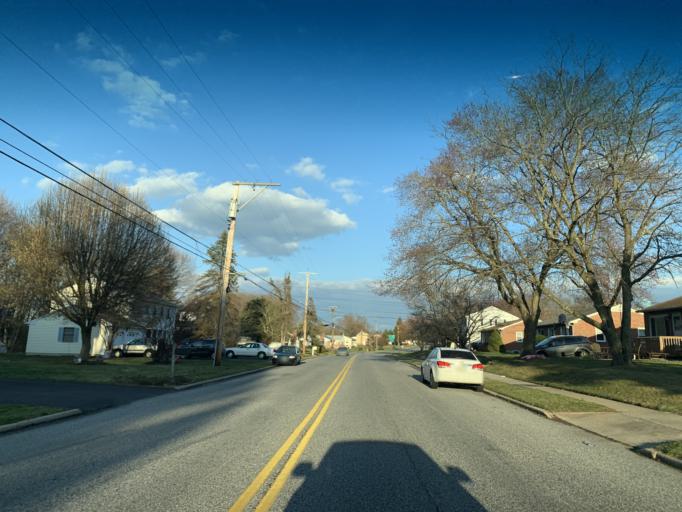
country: US
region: Maryland
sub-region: Harford County
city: Aberdeen
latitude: 39.5275
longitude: -76.1764
